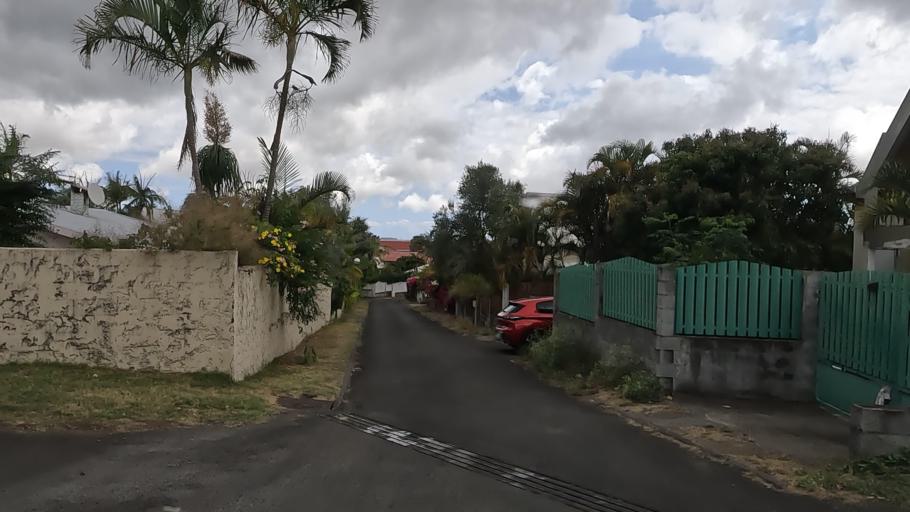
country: RE
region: Reunion
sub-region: Reunion
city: Le Tampon
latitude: -21.2741
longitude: 55.5029
